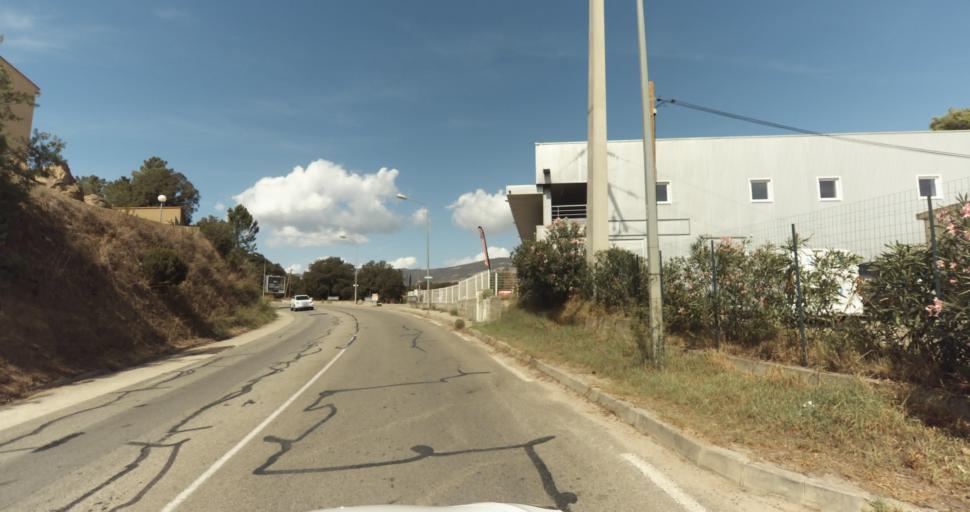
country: FR
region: Corsica
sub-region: Departement de la Corse-du-Sud
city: Afa
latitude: 41.9548
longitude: 8.7839
